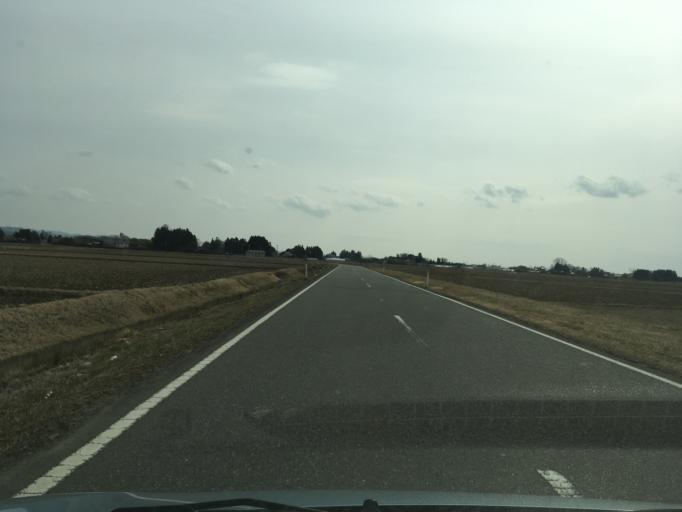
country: JP
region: Miyagi
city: Wakuya
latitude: 38.7259
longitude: 141.2399
